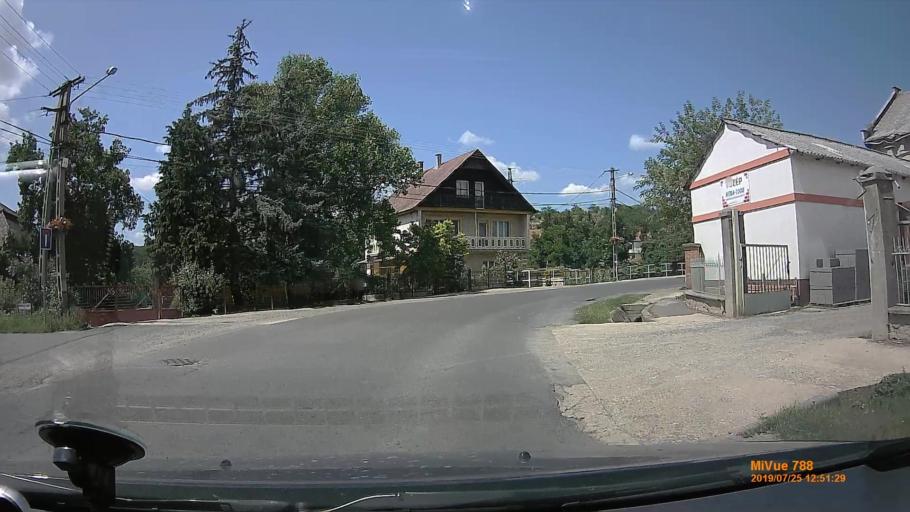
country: HU
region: Borsod-Abauj-Zemplen
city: Abaujszanto
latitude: 48.2842
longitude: 21.1819
